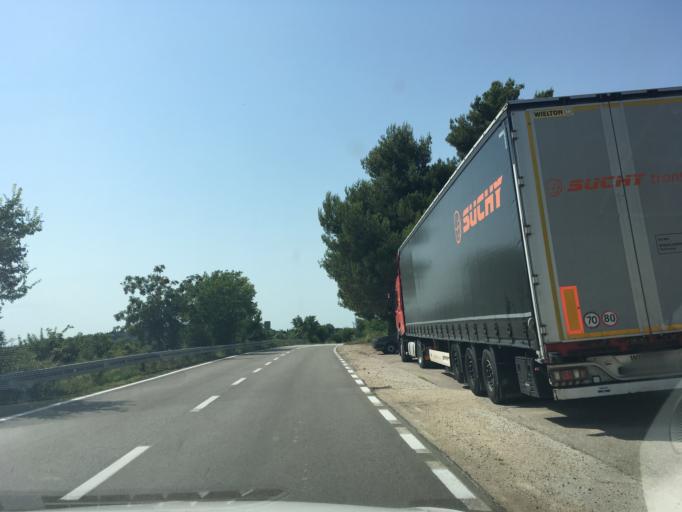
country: HR
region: Zadarska
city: Benkovac
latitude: 44.0233
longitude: 15.6201
